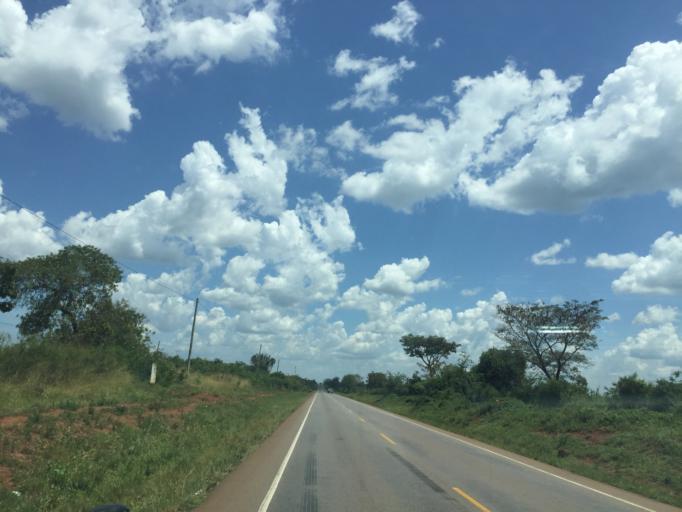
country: UG
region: Central Region
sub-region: Nakasongola District
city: Nakasongola
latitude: 1.3677
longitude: 32.3577
